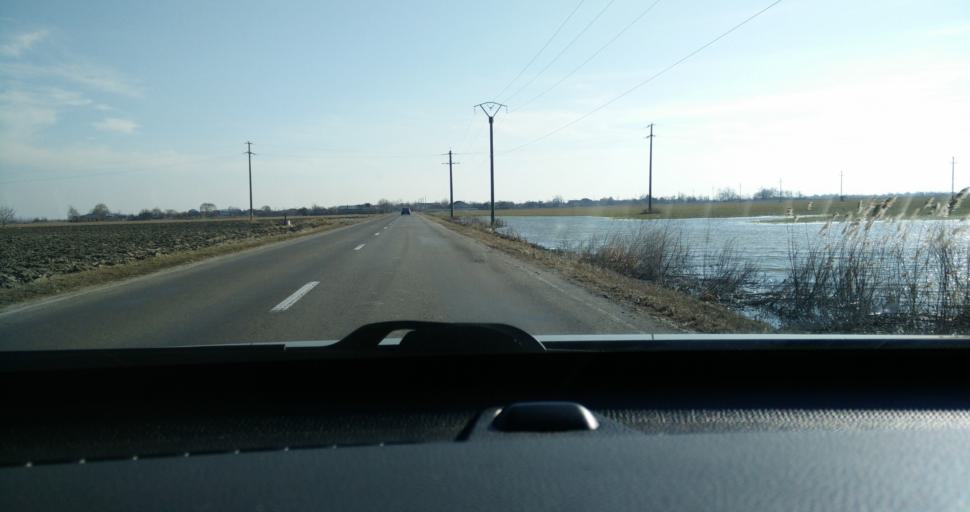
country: RO
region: Vrancea
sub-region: Comuna Nanesti
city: Nanesti
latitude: 45.5593
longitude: 27.4998
